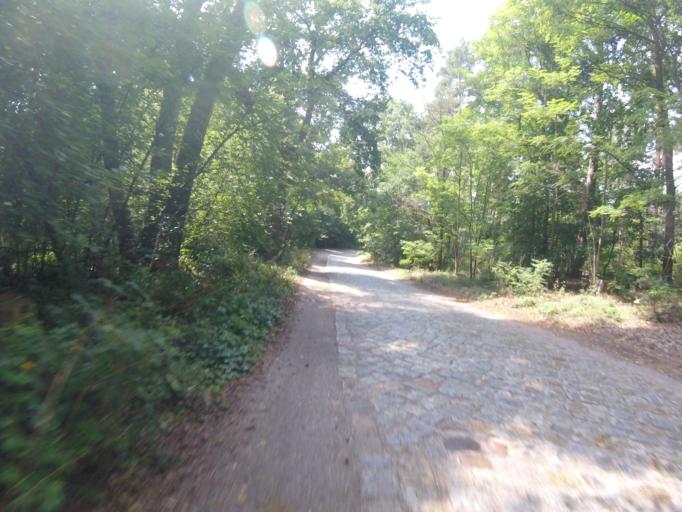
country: DE
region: Brandenburg
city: Schwerin
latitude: 52.1925
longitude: 13.5881
